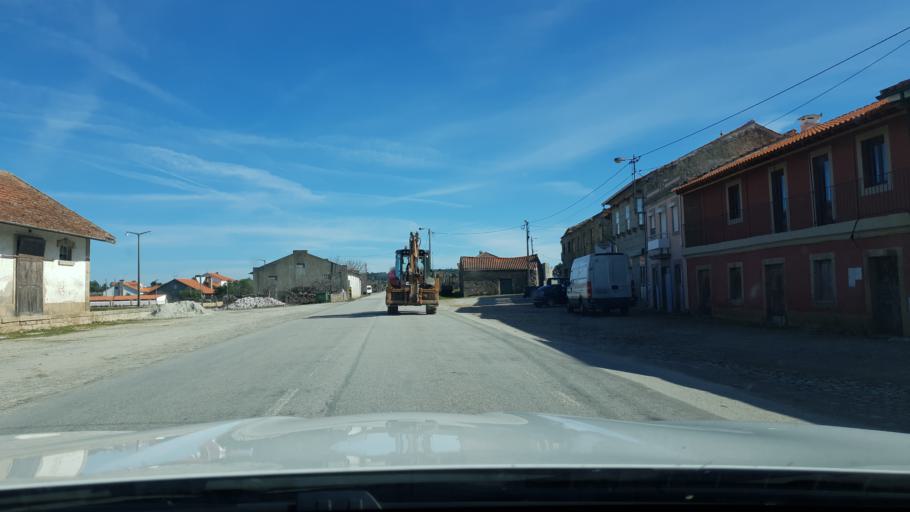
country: PT
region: Braganca
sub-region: Freixo de Espada A Cinta
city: Freixo de Espada a Cinta
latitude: 41.1825
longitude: -6.8857
